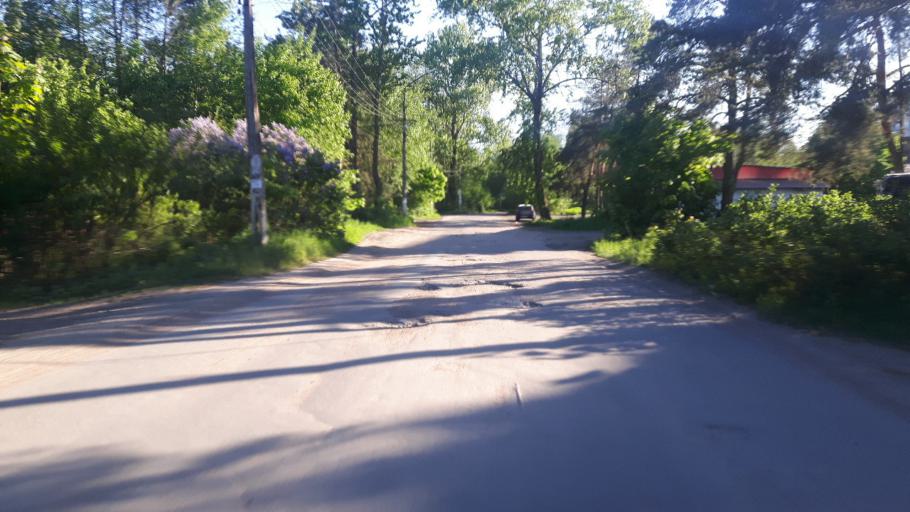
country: RU
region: St.-Petersburg
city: Bol'shaya Izhora
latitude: 59.9440
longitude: 29.5651
